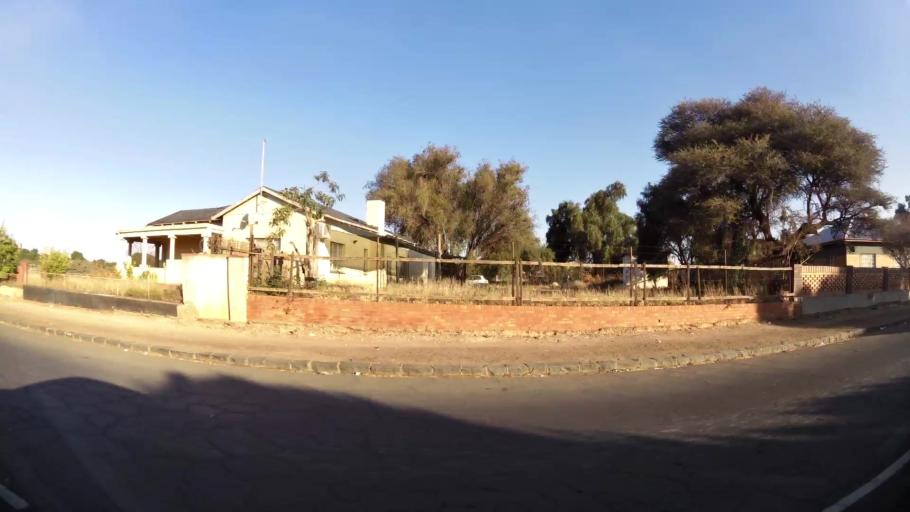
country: ZA
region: Northern Cape
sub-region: Frances Baard District Municipality
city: Kimberley
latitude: -28.7353
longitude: 24.7458
